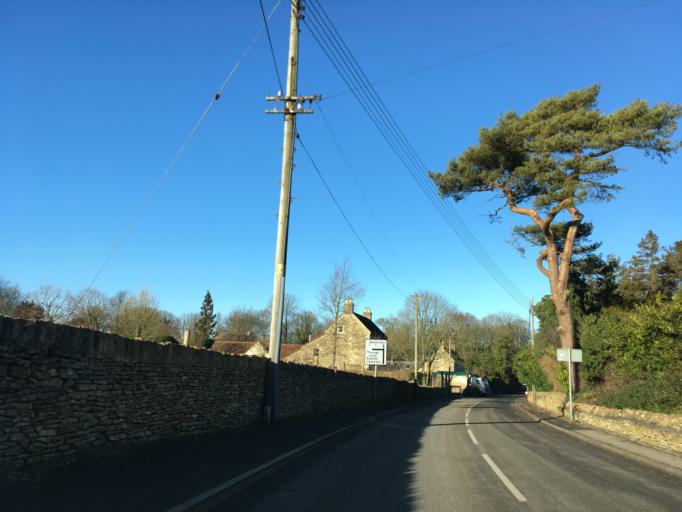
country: GB
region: England
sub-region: Wiltshire
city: Nettleton
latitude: 51.5276
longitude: -2.2767
